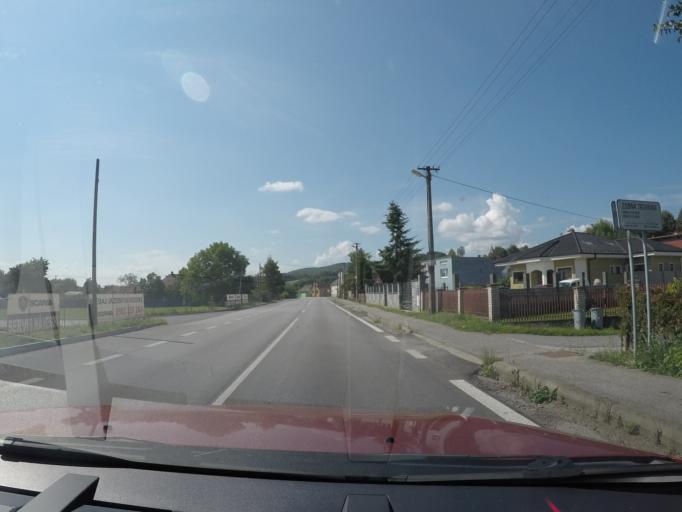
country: SK
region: Presovsky
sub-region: Okres Presov
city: Presov
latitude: 48.8783
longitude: 21.2463
